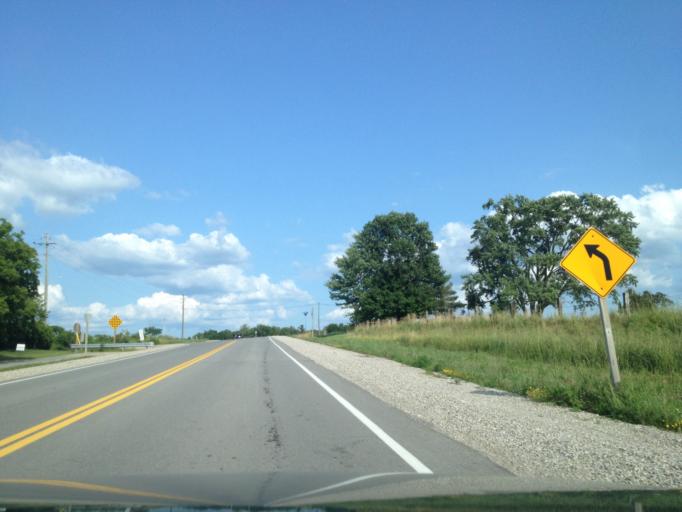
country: CA
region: Ontario
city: Aylmer
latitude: 42.7590
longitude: -80.8331
